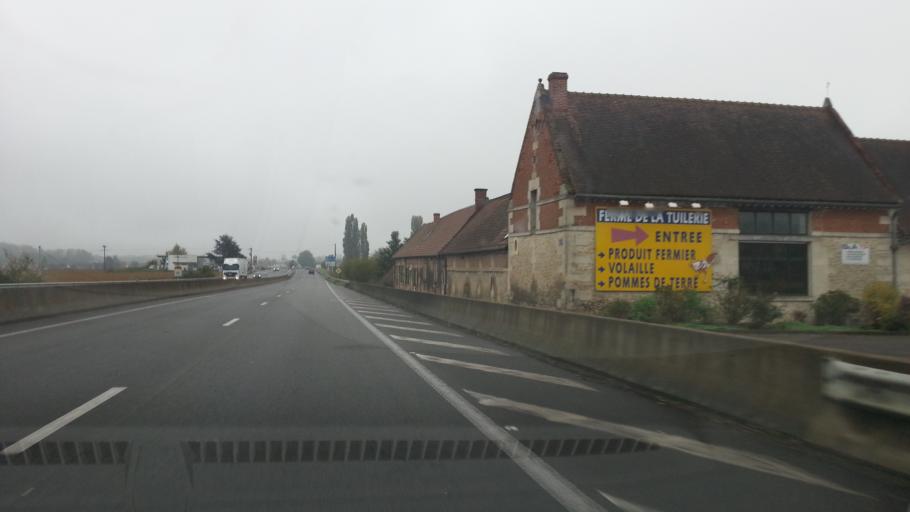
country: FR
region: Picardie
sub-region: Departement de l'Oise
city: Breuil-le-Vert
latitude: 49.3474
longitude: 2.4303
